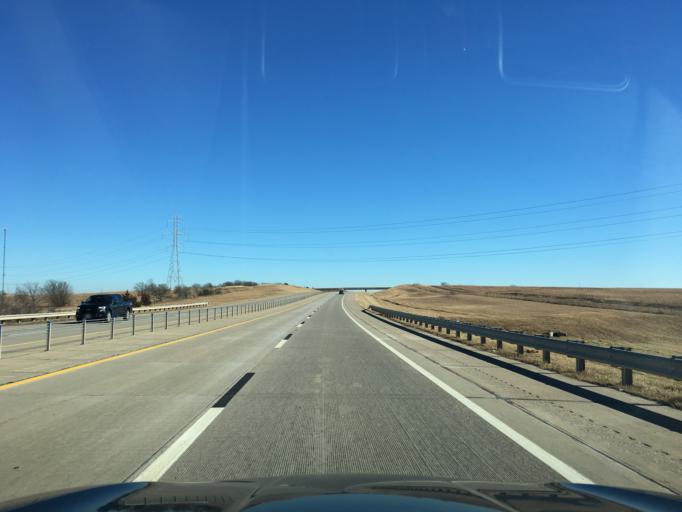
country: US
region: Oklahoma
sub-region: Noble County
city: Perry
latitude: 36.3921
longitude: -97.1107
